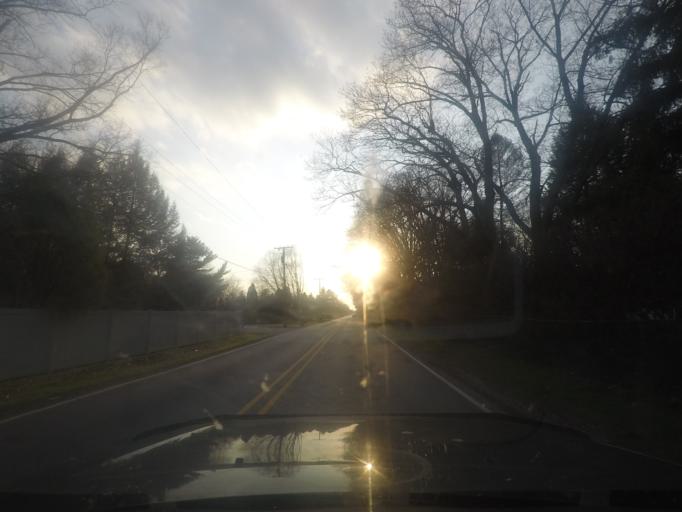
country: US
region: Indiana
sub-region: LaPorte County
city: LaPorte
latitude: 41.5914
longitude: -86.7094
